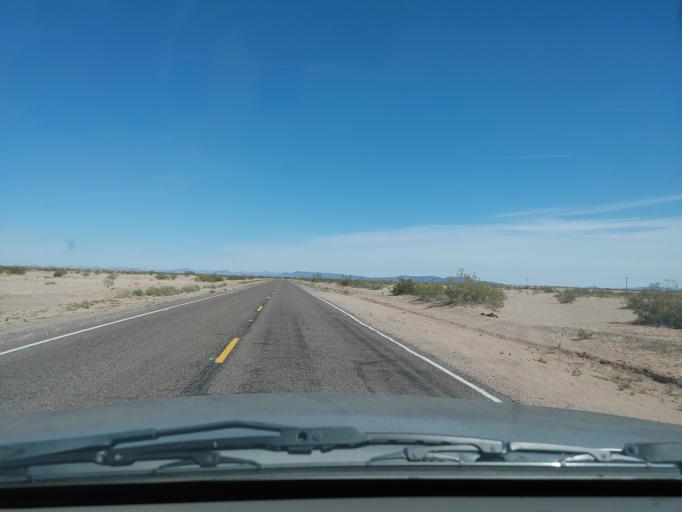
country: US
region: Arizona
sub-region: Maricopa County
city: Gila Bend
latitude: 32.8663
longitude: -113.2129
